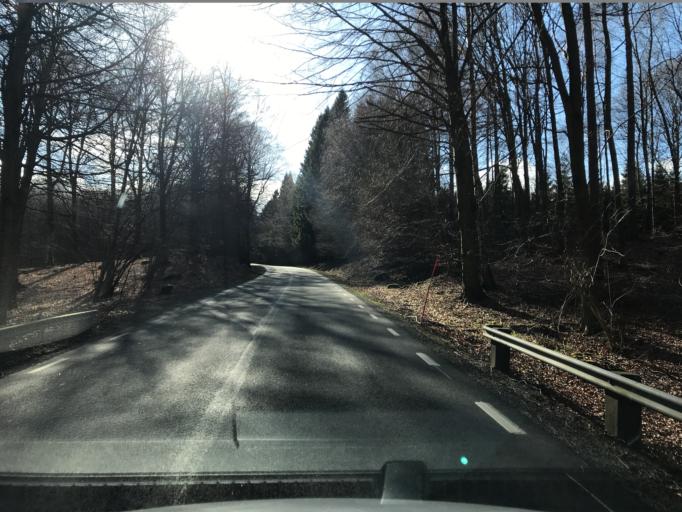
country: SE
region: Skane
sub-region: Kristianstads Kommun
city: Degeberga
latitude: 55.8778
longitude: 14.0045
